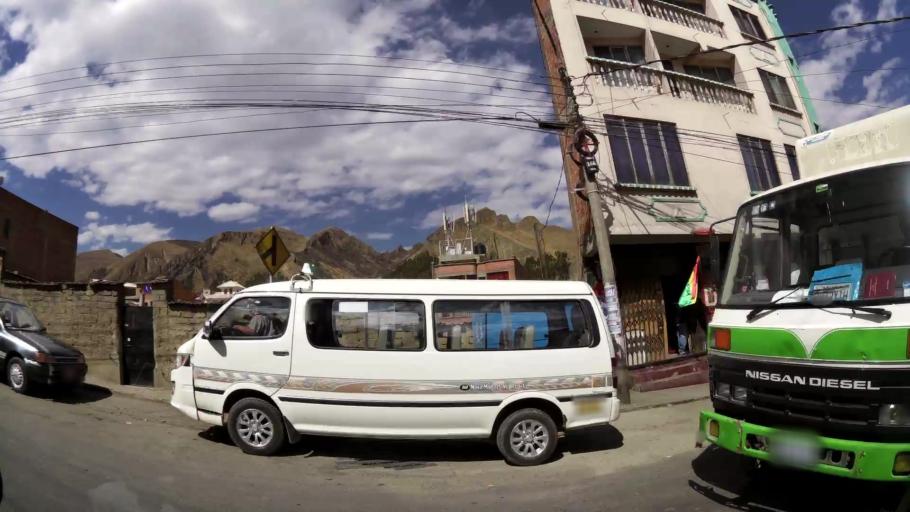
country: BO
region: La Paz
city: La Paz
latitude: -16.4657
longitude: -68.1106
